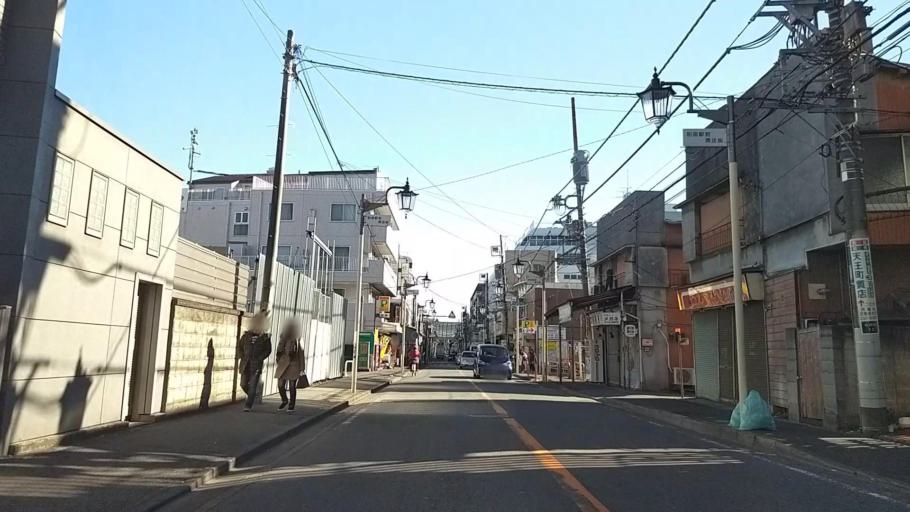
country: JP
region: Kanagawa
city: Yokohama
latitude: 35.4636
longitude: 139.5858
